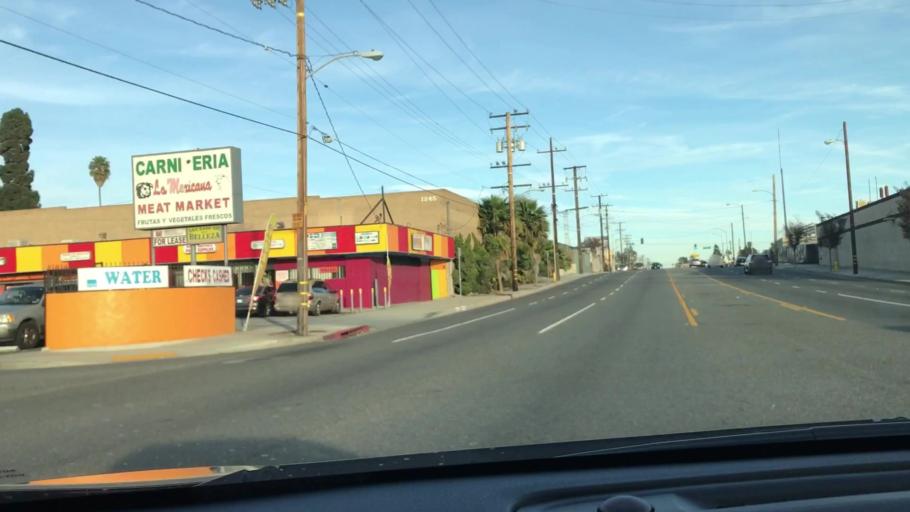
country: US
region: California
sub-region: Los Angeles County
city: West Athens
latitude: 33.9165
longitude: -118.2988
